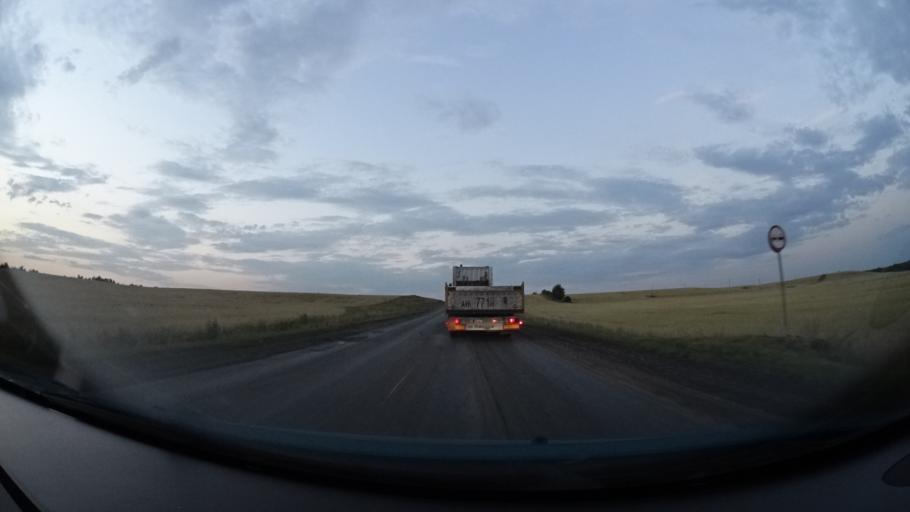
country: RU
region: Tatarstan
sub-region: Bavlinskiy Rayon
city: Bavly
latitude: 54.2933
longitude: 53.0041
